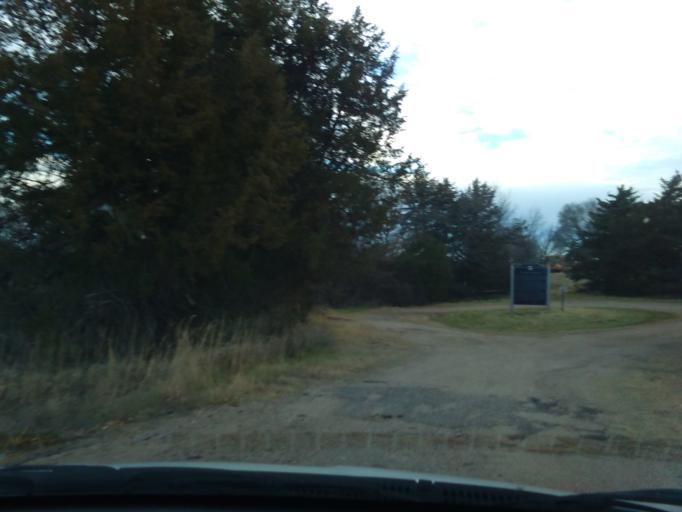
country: US
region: Nebraska
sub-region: Phelps County
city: Holdrege
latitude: 40.3072
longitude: -99.3460
